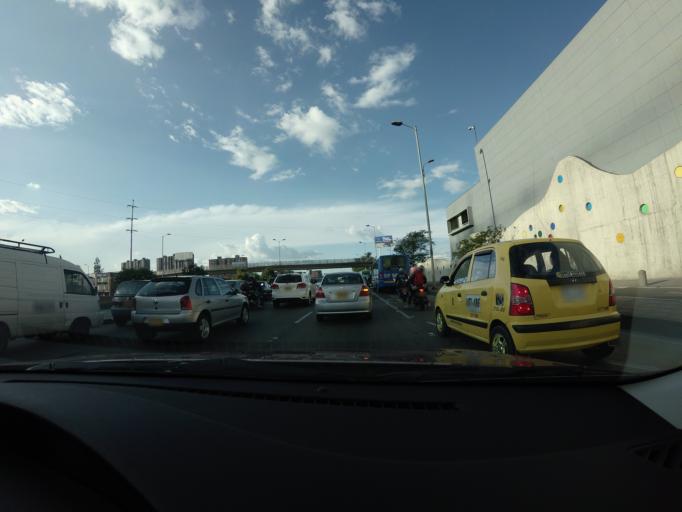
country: CO
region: Bogota D.C.
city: Bogota
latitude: 4.6559
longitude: -74.0777
